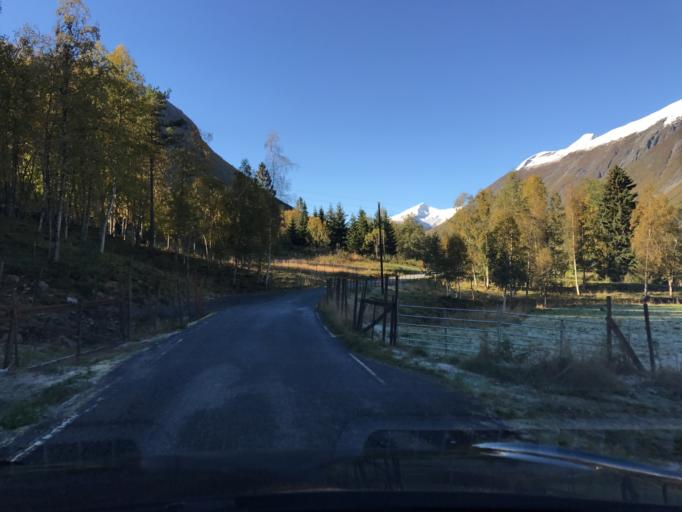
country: NO
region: More og Romsdal
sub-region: Norddal
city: Valldal
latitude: 62.3304
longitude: 7.3843
